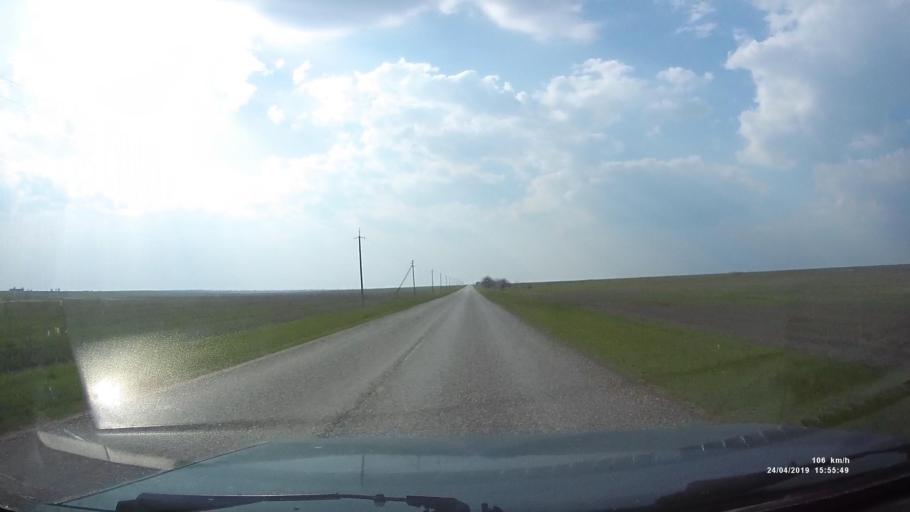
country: RU
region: Kalmykiya
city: Yashalta
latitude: 46.5931
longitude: 42.5417
